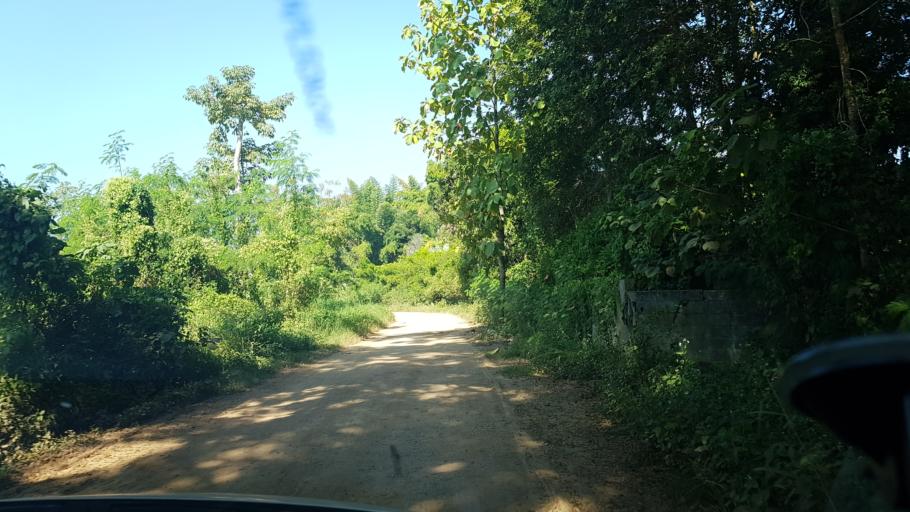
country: TH
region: Chiang Rai
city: Chiang Rai
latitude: 19.9013
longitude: 99.7953
